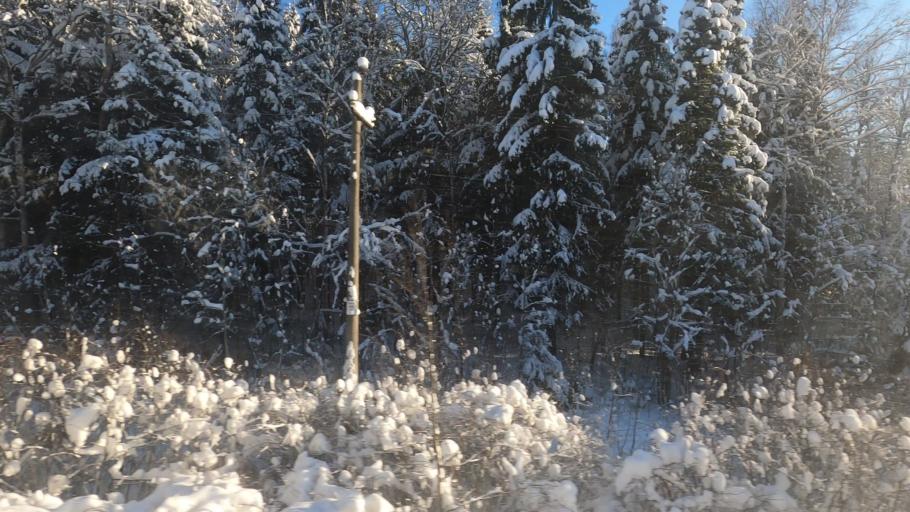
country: RU
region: Moskovskaya
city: Novo-Nikol'skoye
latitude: 56.5512
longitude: 37.5633
